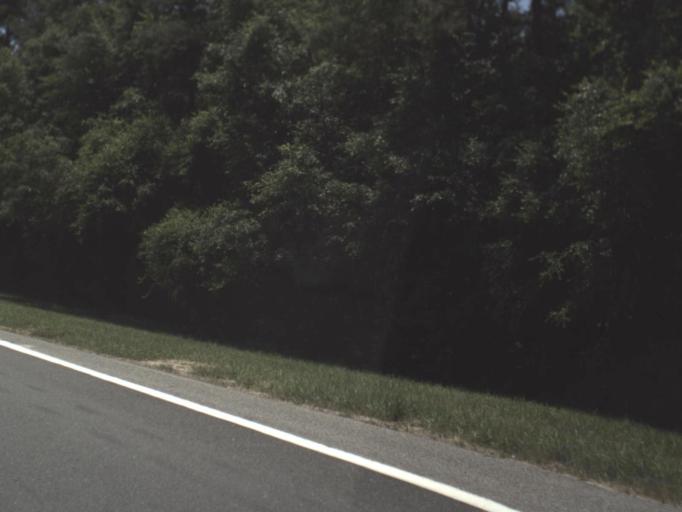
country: US
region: Florida
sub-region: Suwannee County
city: Live Oak
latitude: 30.3829
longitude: -83.1745
